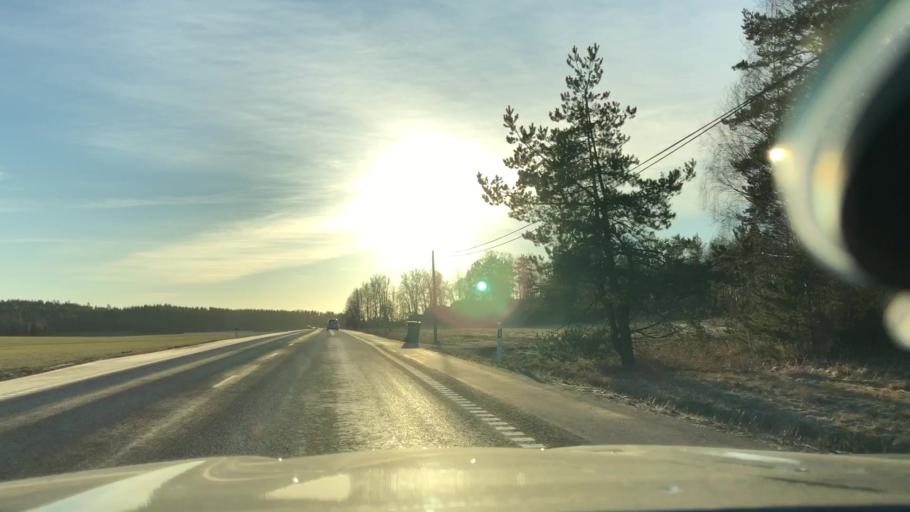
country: SE
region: Soedermanland
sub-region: Trosa Kommun
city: Vagnharad
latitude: 59.0319
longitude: 17.5968
